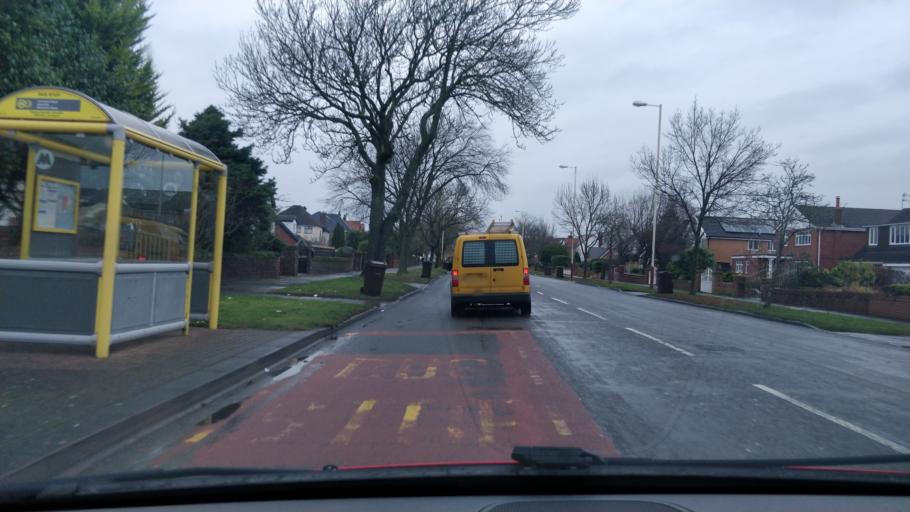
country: GB
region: England
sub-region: Sefton
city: Formby
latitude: 53.5894
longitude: -3.0399
